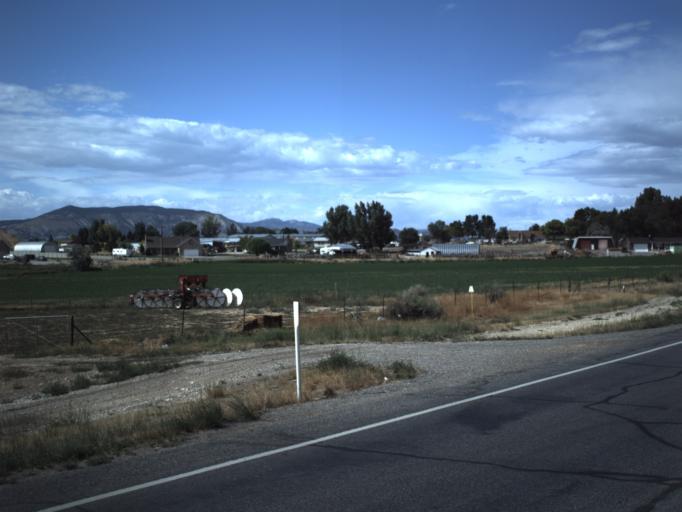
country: US
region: Utah
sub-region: Sanpete County
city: Manti
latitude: 39.1878
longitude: -111.6937
